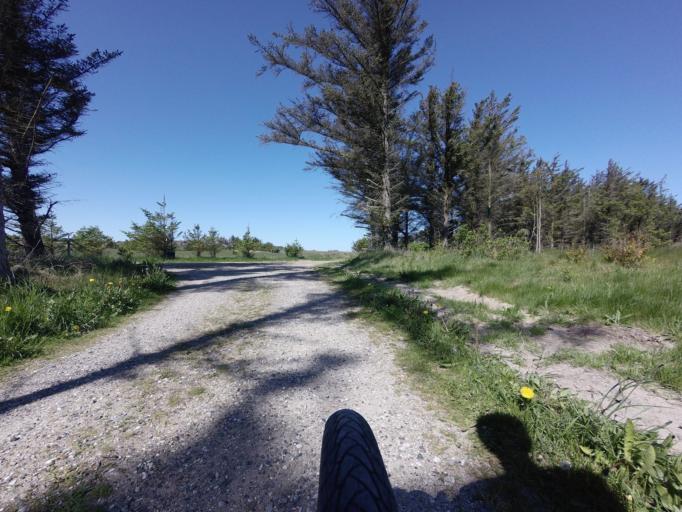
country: DK
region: North Denmark
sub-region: Jammerbugt Kommune
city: Pandrup
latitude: 57.3148
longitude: 9.6661
